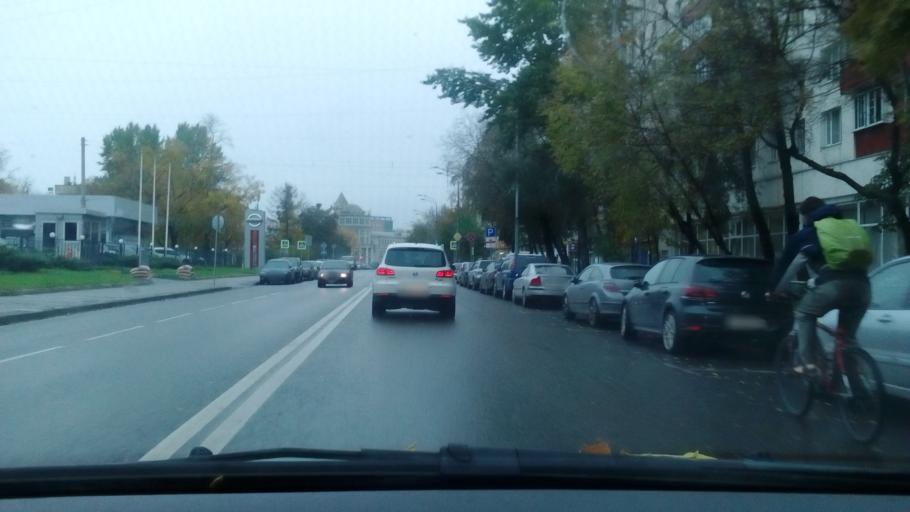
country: RU
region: Moscow
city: Mar'ina Roshcha
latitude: 55.7945
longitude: 37.5767
